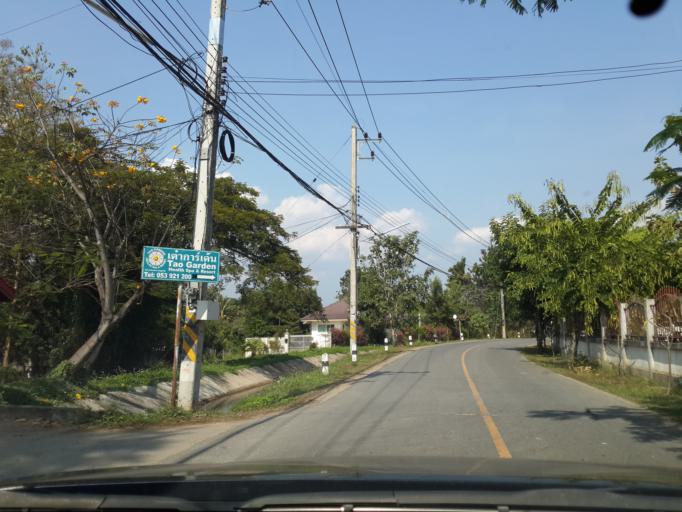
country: TH
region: Chiang Mai
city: San Sai
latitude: 18.8869
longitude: 99.1237
